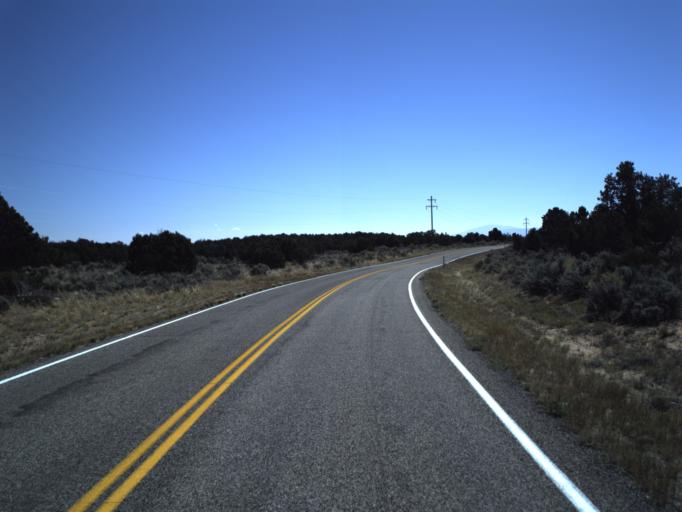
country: US
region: Utah
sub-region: Wayne County
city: Loa
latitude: 37.8709
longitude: -111.4433
